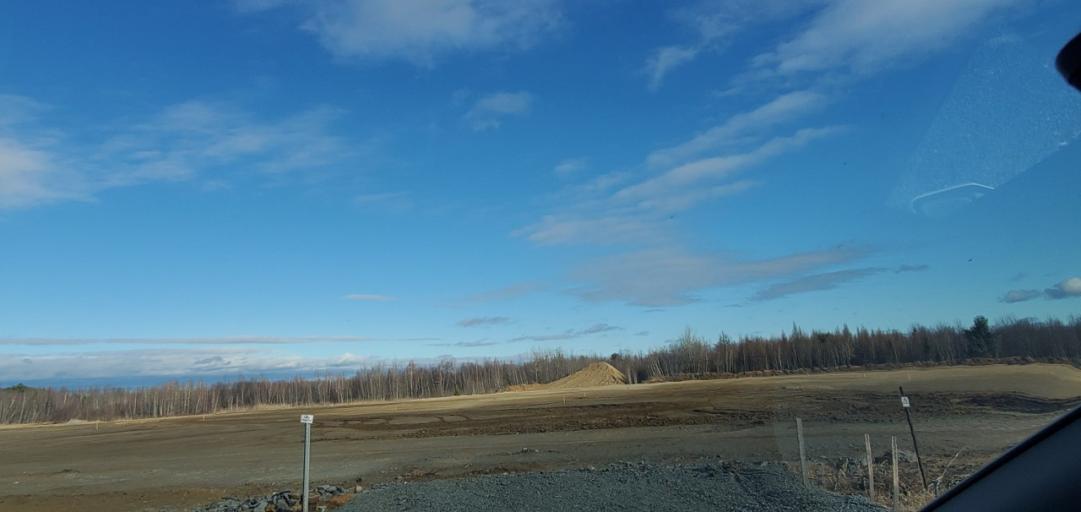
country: CA
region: Quebec
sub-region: Centre-du-Quebec
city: Drummondville
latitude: 45.8249
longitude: -72.4381
